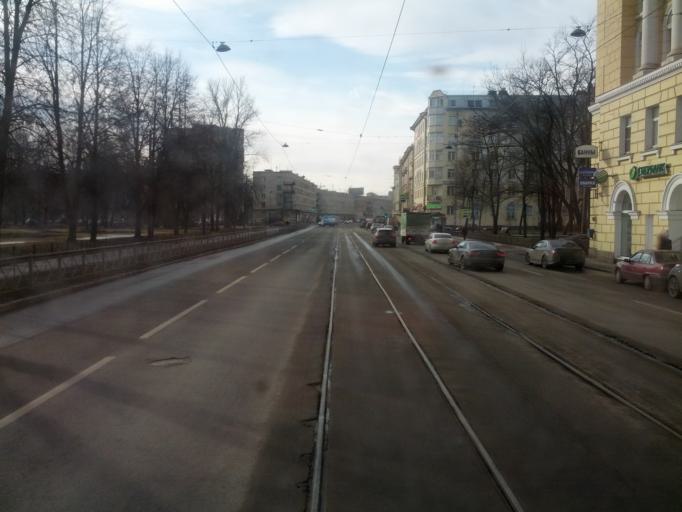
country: RU
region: Leningrad
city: Kalininskiy
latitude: 59.9487
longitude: 30.4145
